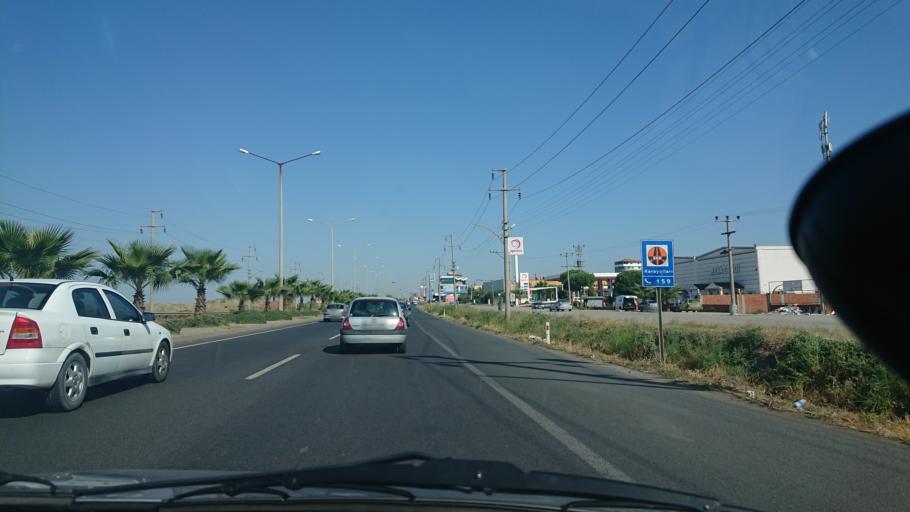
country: TR
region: Manisa
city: Turgutlu
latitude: 38.4957
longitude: 27.7303
